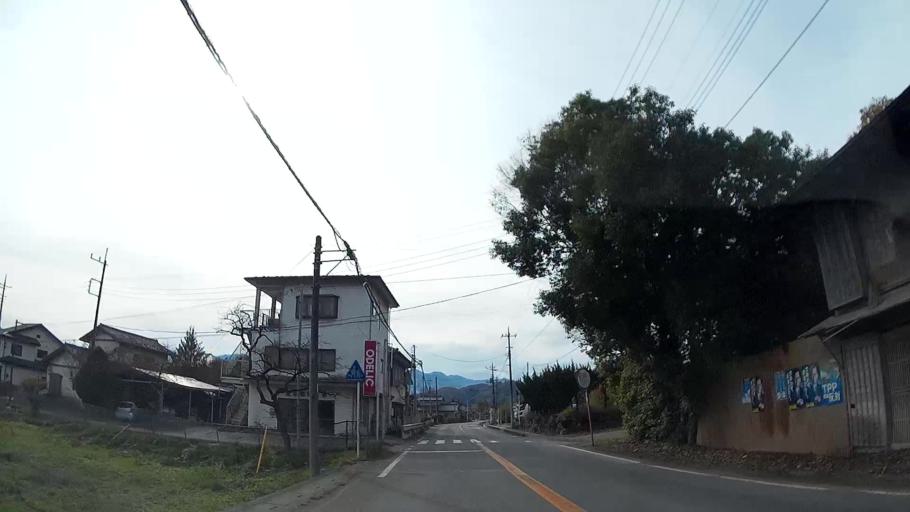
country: JP
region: Saitama
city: Chichibu
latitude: 36.0192
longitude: 139.0391
